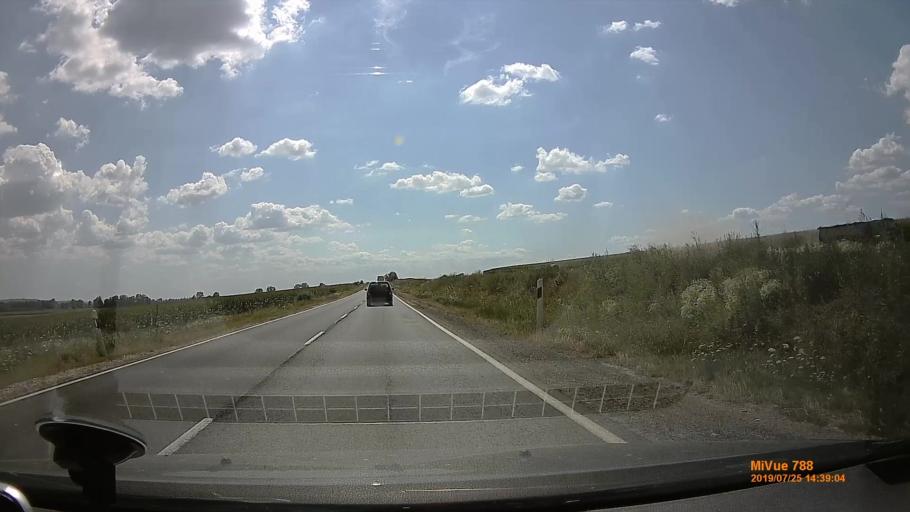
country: HU
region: Borsod-Abauj-Zemplen
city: Halmaj
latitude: 48.3020
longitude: 21.0579
